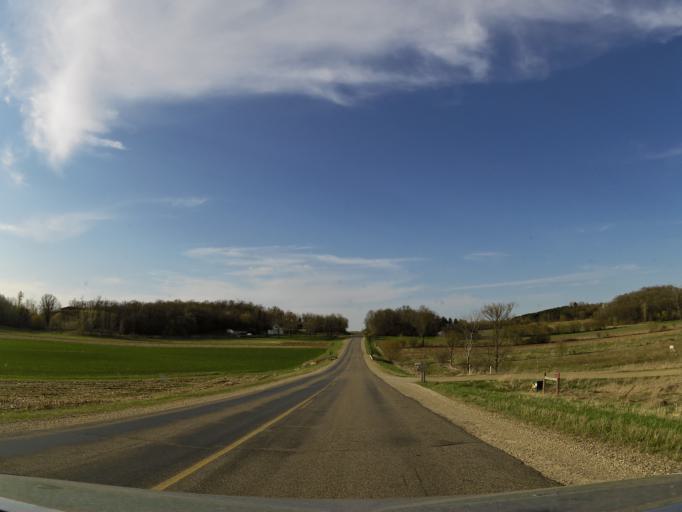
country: US
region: Wisconsin
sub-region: Pierce County
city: River Falls
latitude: 44.7521
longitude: -92.6396
